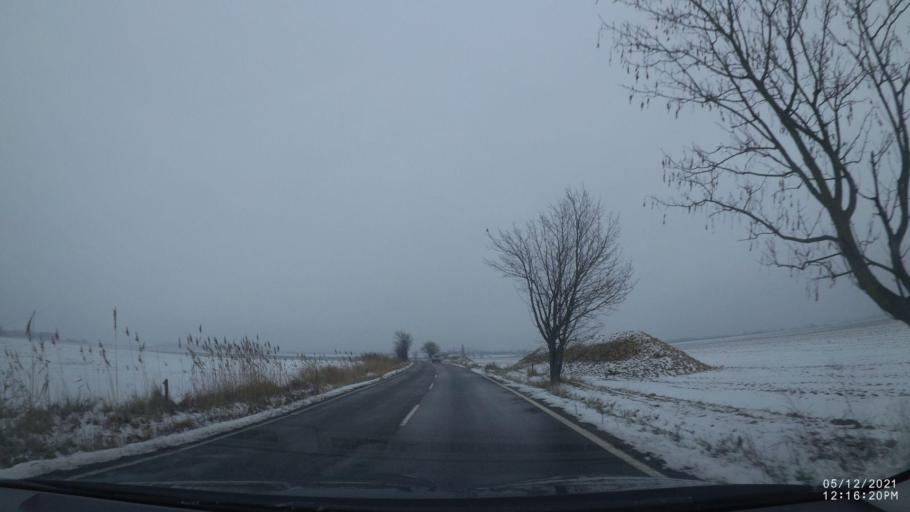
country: CZ
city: Ceske Mezirici
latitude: 50.3072
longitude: 16.0586
